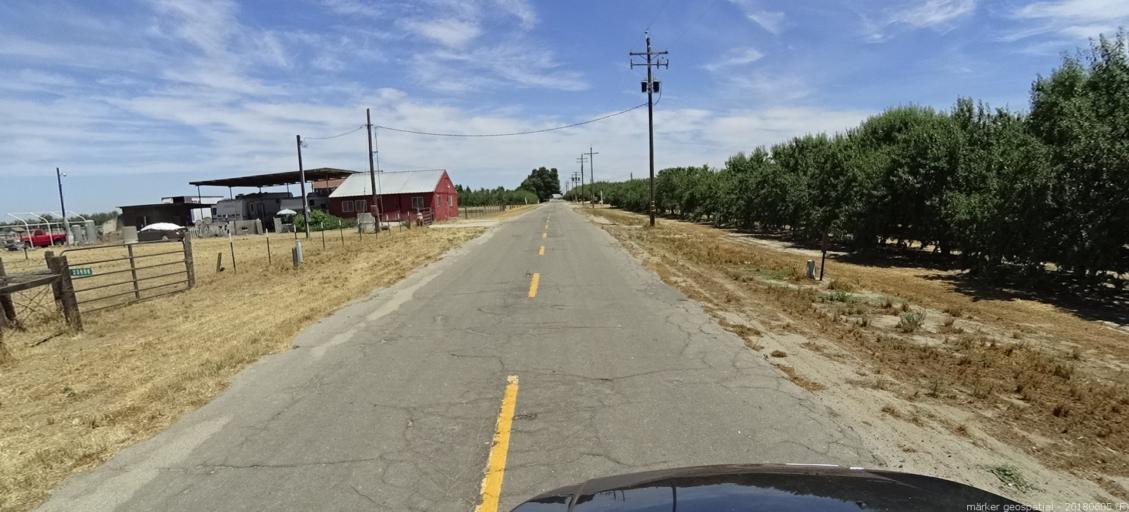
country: US
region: California
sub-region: Madera County
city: Chowchilla
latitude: 37.0926
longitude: -120.4188
